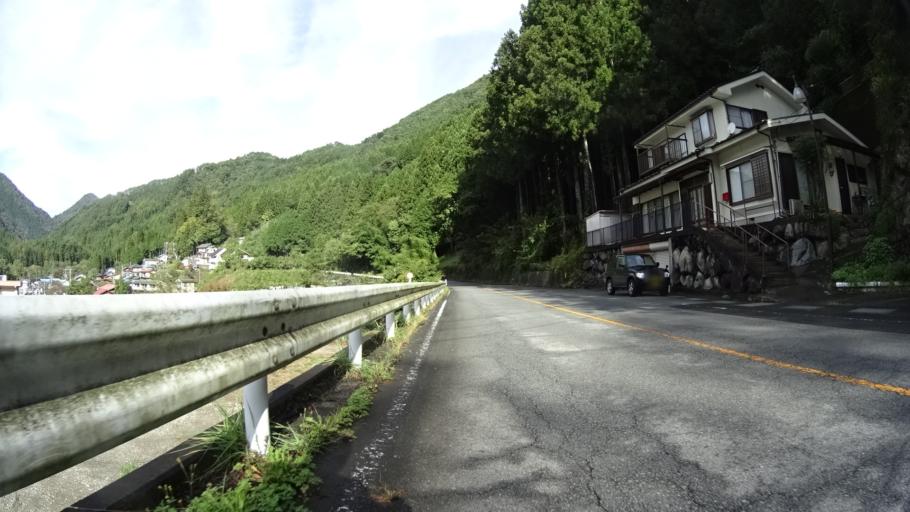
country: JP
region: Yamanashi
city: Otsuki
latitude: 35.7930
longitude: 138.9158
